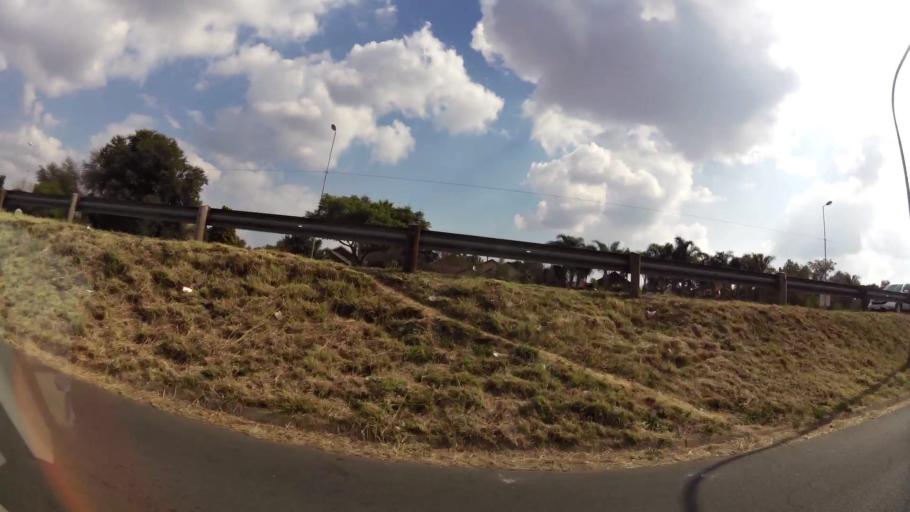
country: ZA
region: Gauteng
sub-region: City of Tshwane Metropolitan Municipality
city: Centurion
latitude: -25.8264
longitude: 28.2558
